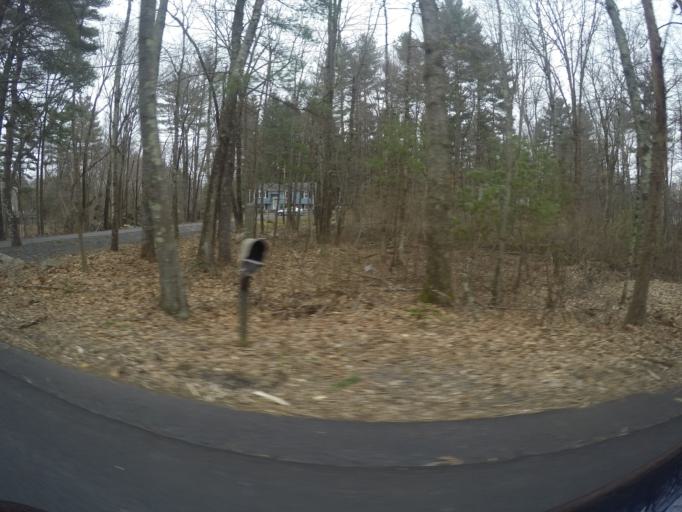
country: US
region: Massachusetts
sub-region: Bristol County
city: Easton
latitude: 42.0405
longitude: -71.1622
